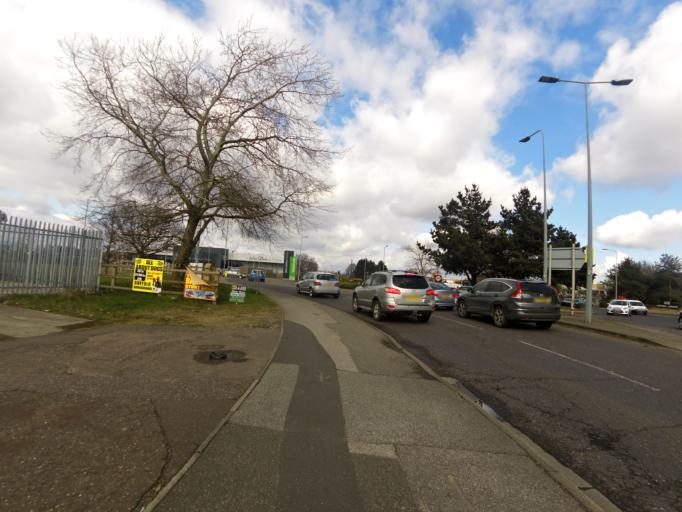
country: GB
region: England
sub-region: Suffolk
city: Kesgrave
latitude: 52.0325
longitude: 1.2037
